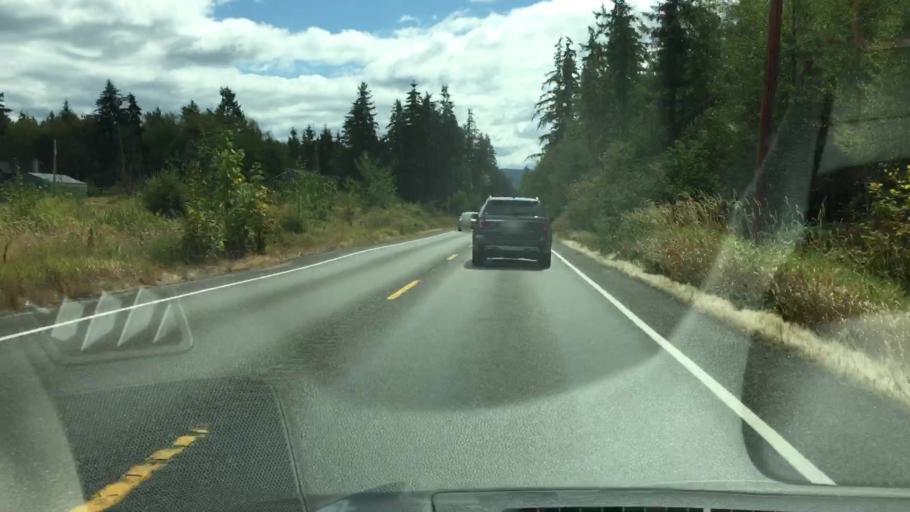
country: US
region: Washington
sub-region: Pierce County
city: Eatonville
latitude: 46.9015
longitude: -122.2977
